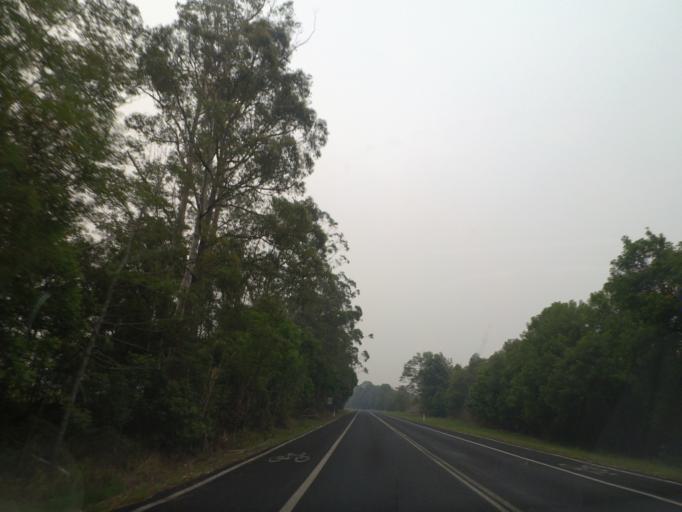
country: AU
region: New South Wales
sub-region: Coffs Harbour
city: Bonville
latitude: -30.3964
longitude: 153.0314
